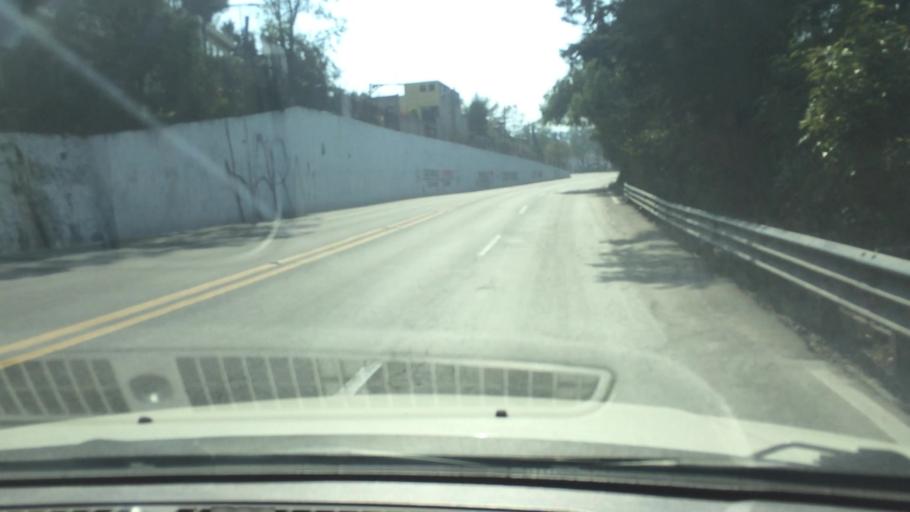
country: MX
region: Mexico City
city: Tlalpan
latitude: 19.2718
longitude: -99.1689
